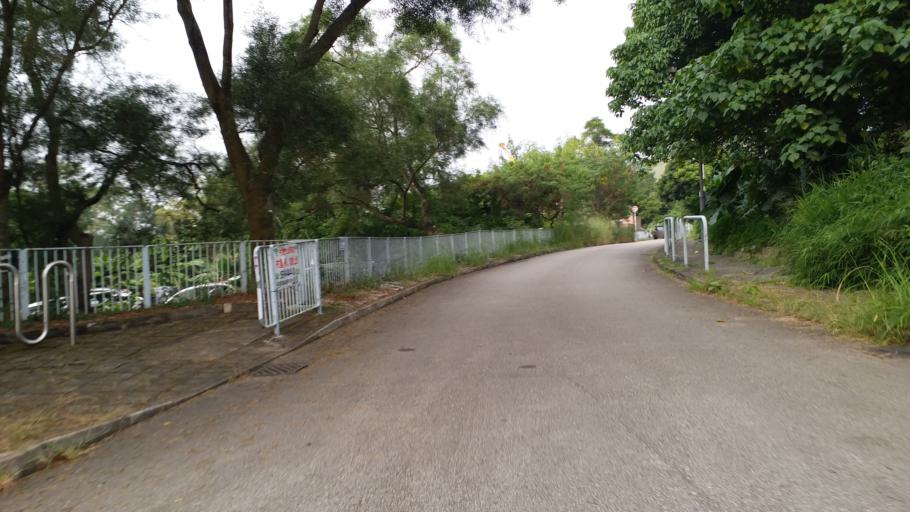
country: HK
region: Yuen Long
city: Yuen Long Kau Hui
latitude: 22.4538
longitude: 114.0107
